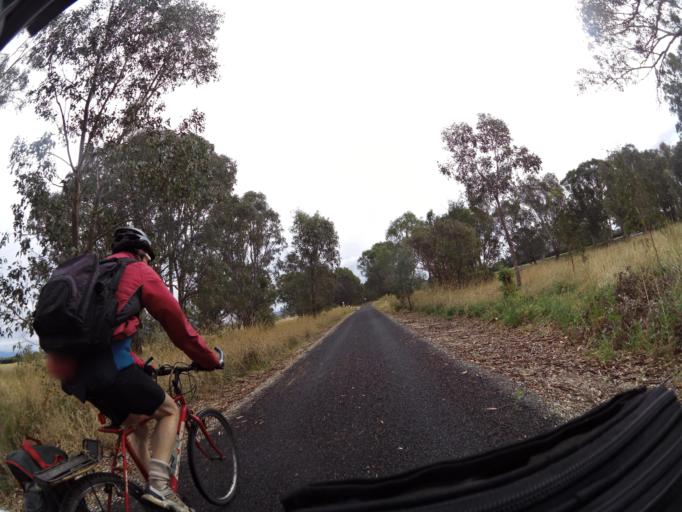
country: AU
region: New South Wales
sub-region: Albury Municipality
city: East Albury
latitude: -36.1403
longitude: 146.9826
